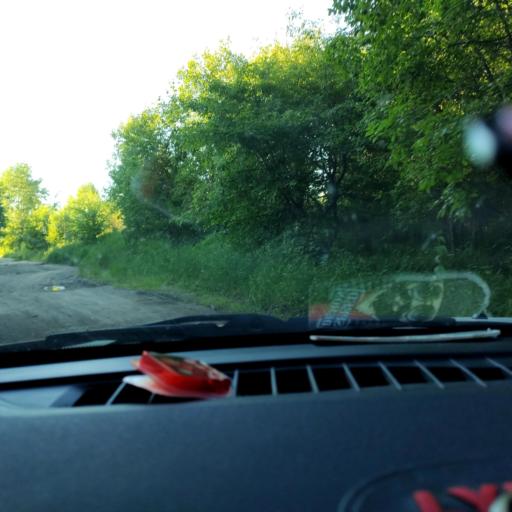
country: RU
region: Perm
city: Froly
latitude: 57.9430
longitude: 56.1991
